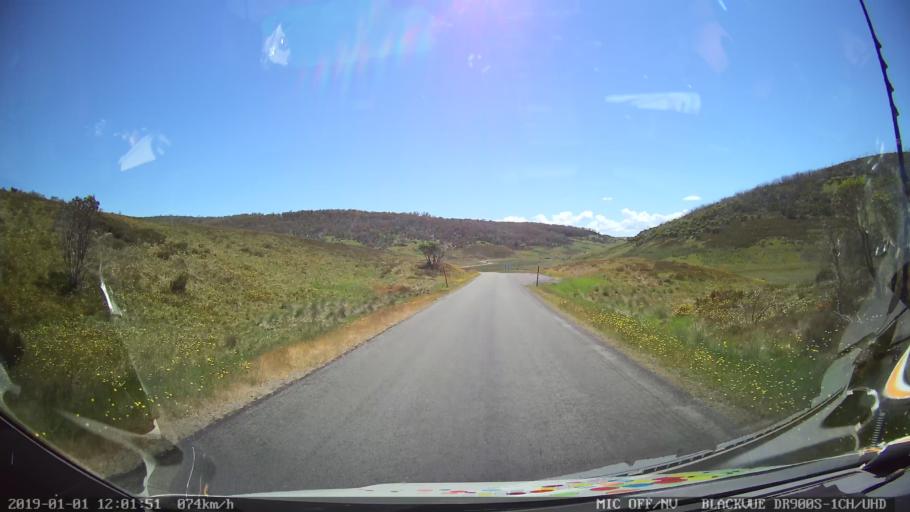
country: AU
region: New South Wales
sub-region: Snowy River
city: Jindabyne
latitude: -35.8773
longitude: 148.4725
